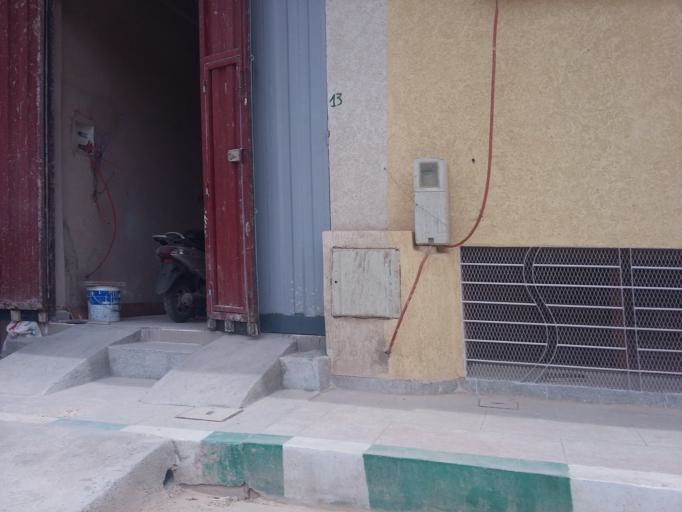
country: MA
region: Fes-Boulemane
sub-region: Fes
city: Fes
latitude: 34.0006
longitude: -5.0084
